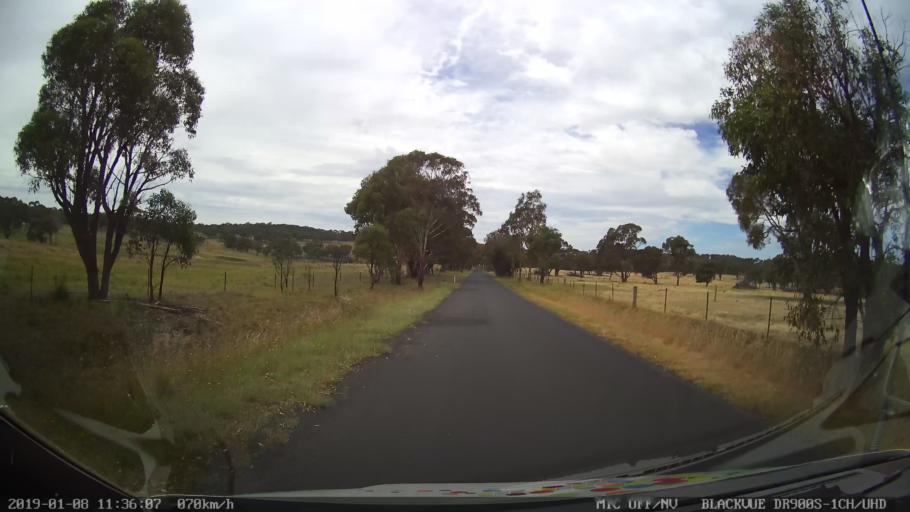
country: AU
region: New South Wales
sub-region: Guyra
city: Guyra
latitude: -30.3433
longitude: 151.5410
